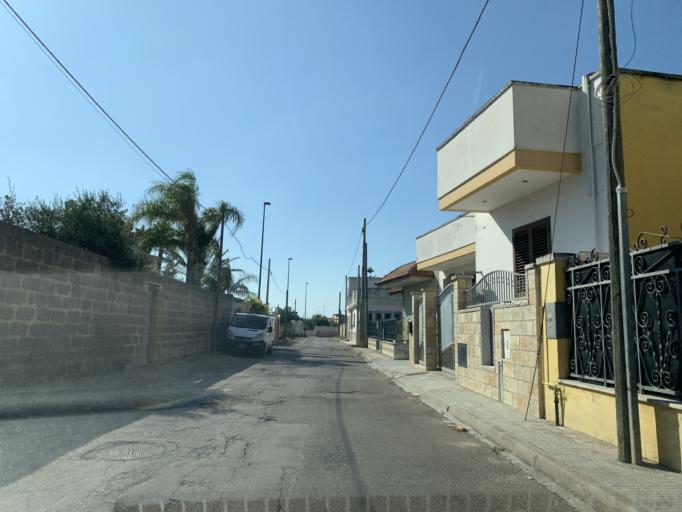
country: IT
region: Apulia
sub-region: Provincia di Lecce
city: Copertino
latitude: 40.2670
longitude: 18.0371
